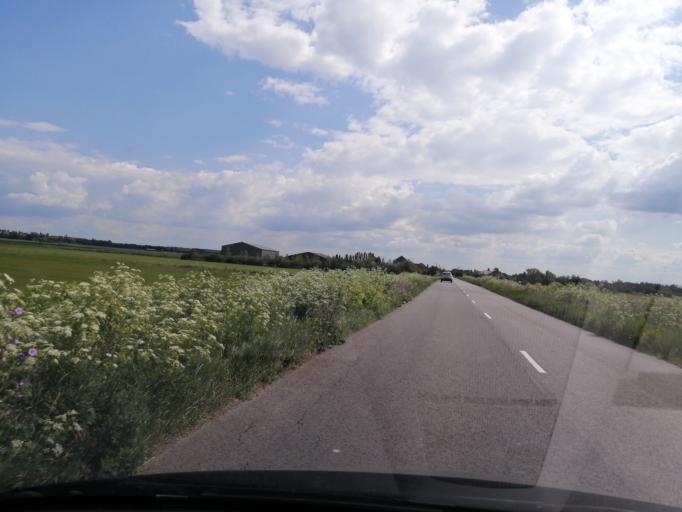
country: GB
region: England
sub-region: Cambridgeshire
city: Ramsey
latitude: 52.4613
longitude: -0.1558
